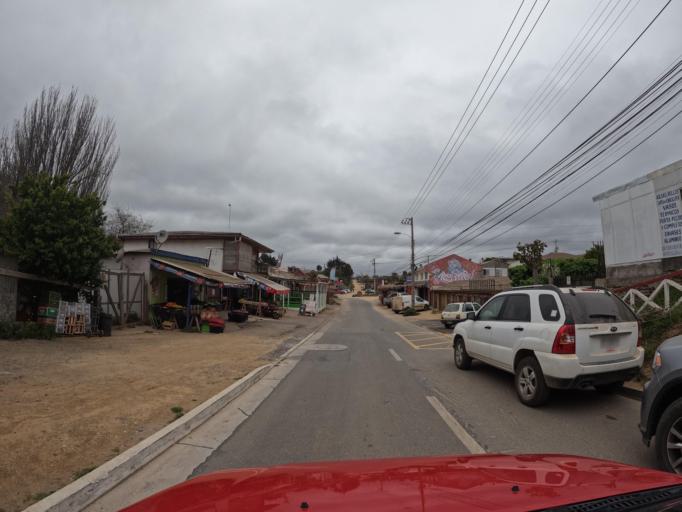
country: CL
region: O'Higgins
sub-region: Provincia de Colchagua
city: Santa Cruz
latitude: -34.3874
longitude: -72.0078
